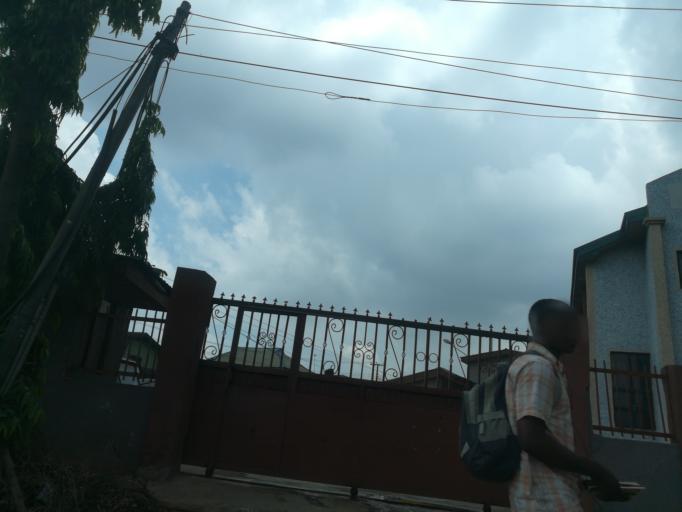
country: NG
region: Lagos
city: Ojota
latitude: 6.6003
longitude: 3.3649
